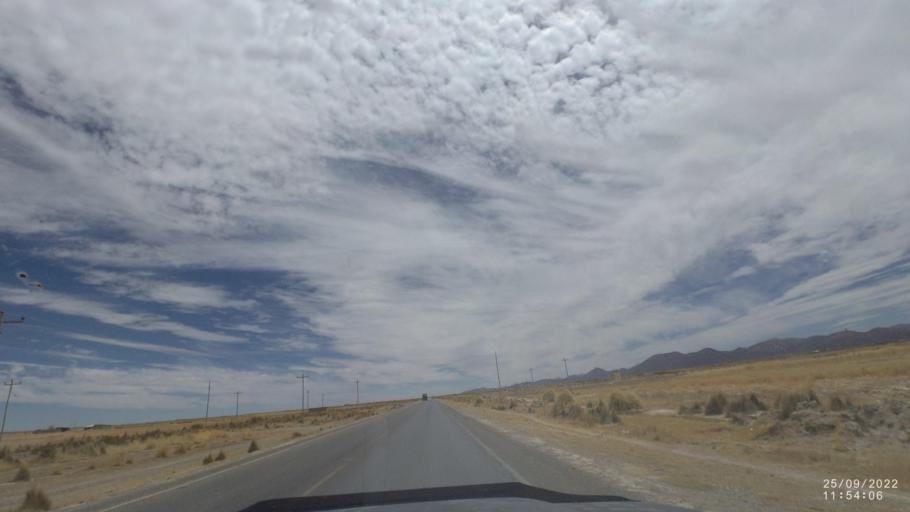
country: BO
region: Oruro
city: Challapata
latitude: -18.8798
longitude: -66.7898
